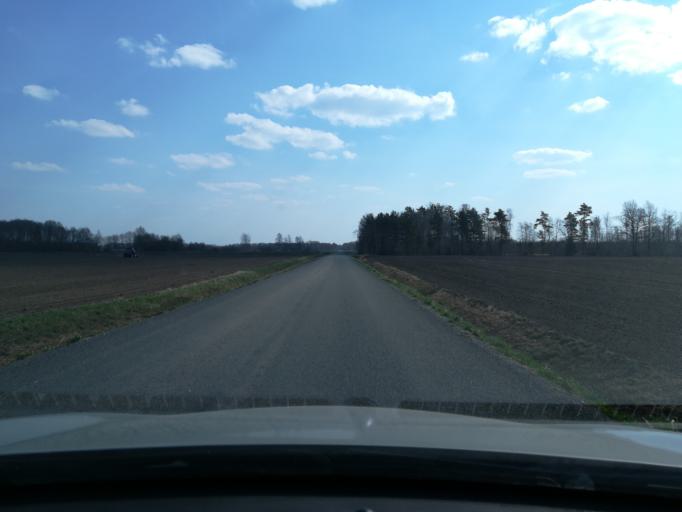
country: EE
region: Harju
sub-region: Saue linn
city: Saue
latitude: 59.3318
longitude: 24.5056
